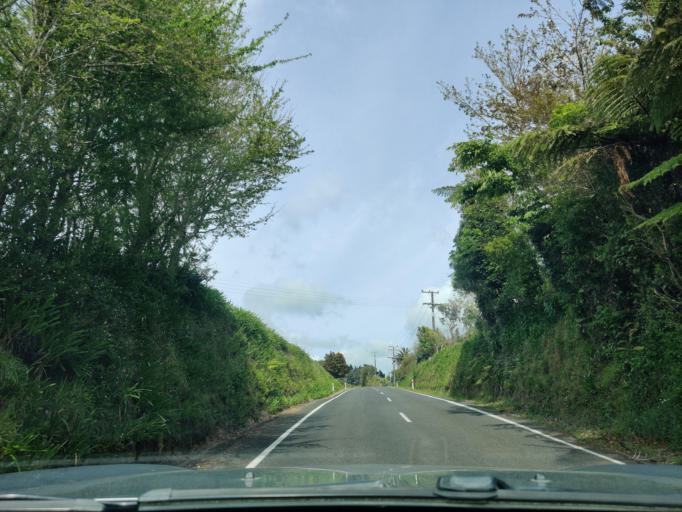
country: NZ
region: Taranaki
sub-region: New Plymouth District
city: New Plymouth
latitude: -39.1150
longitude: 174.0986
